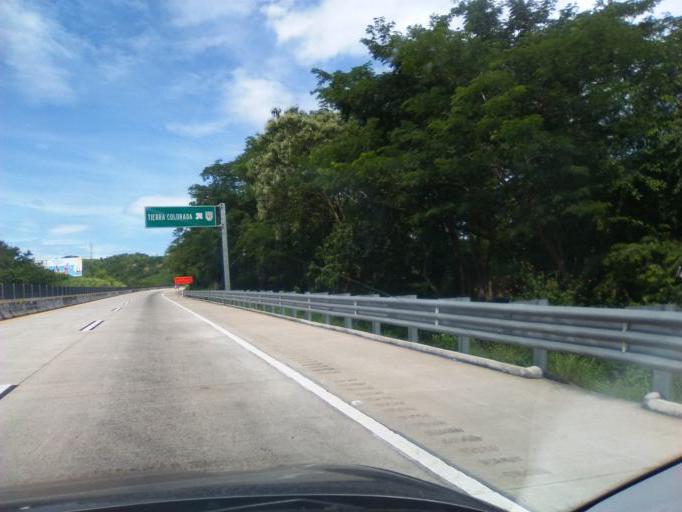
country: MX
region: Guerrero
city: Tierra Colorada
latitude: 17.1668
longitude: -99.5539
